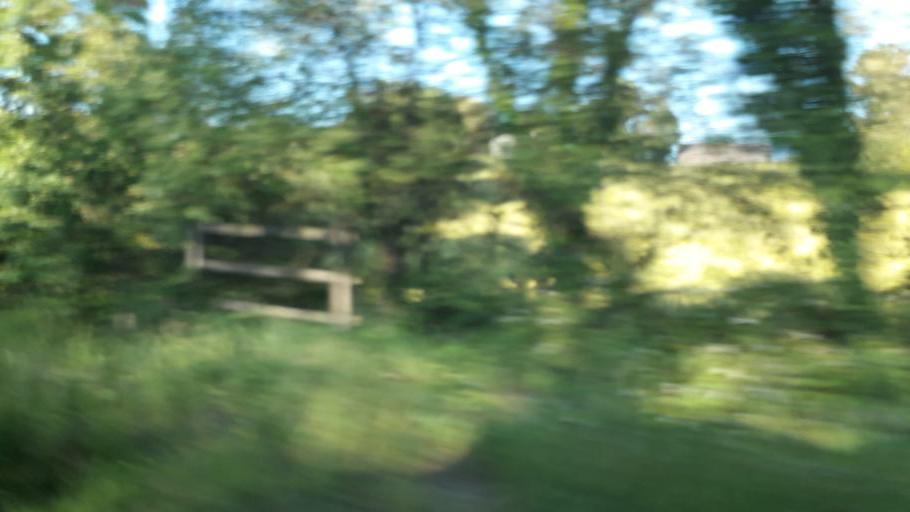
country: IE
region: Leinster
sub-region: Loch Garman
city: Loch Garman
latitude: 52.3475
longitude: -6.5142
